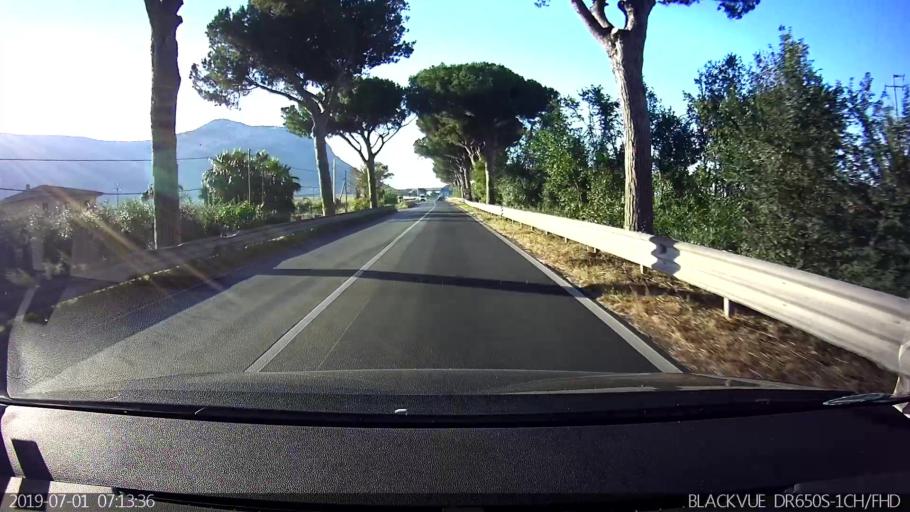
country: IT
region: Latium
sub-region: Provincia di Latina
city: Borgo Hermada
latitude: 41.3247
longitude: 13.1799
